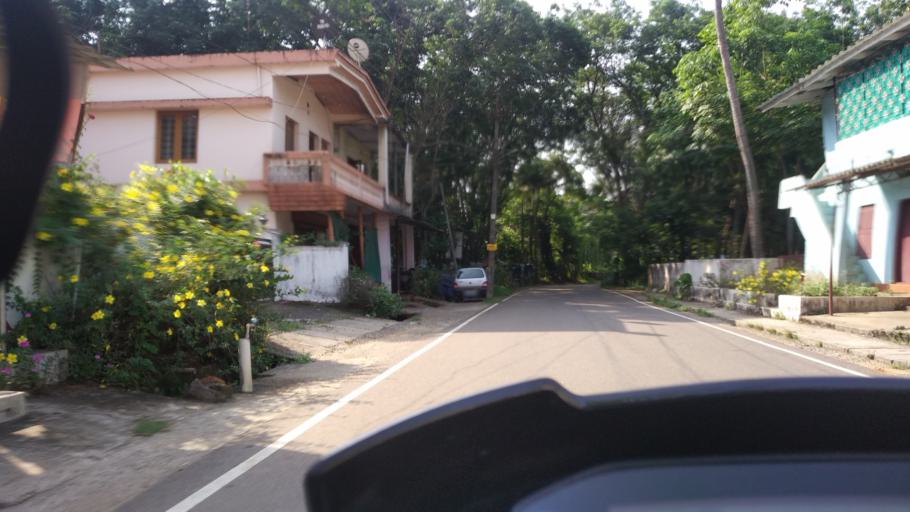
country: IN
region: Kerala
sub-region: Ernakulam
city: Piravam
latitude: 9.8523
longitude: 76.5311
